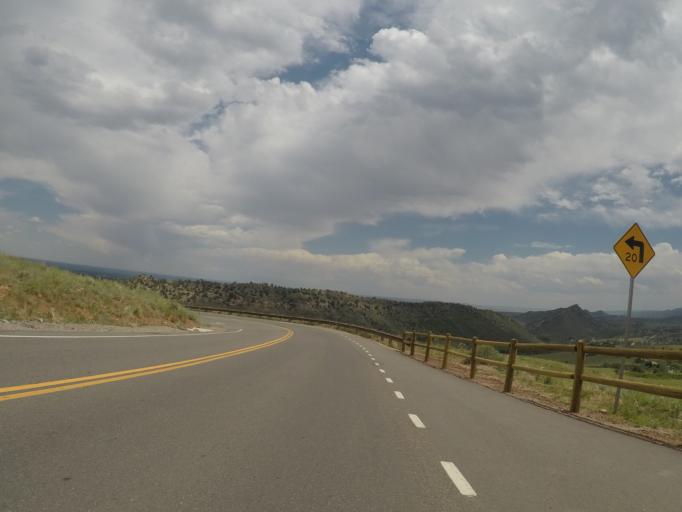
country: US
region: Colorado
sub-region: Jefferson County
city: Indian Hills
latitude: 39.6696
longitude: -105.2022
